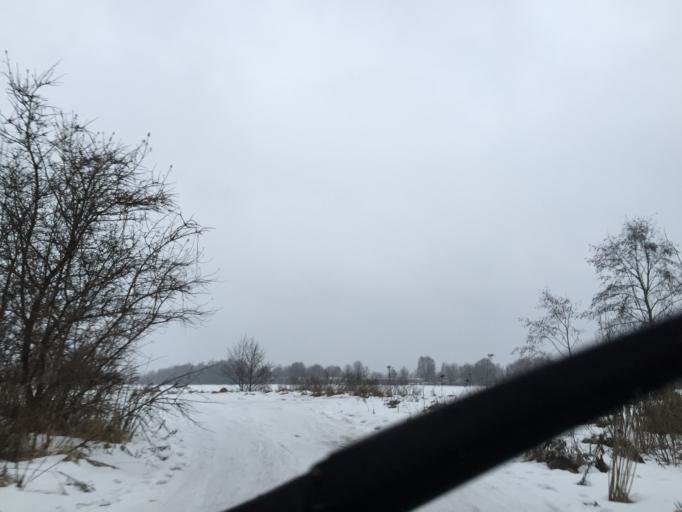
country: LV
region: Riga
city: Riga
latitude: 56.9215
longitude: 24.1321
